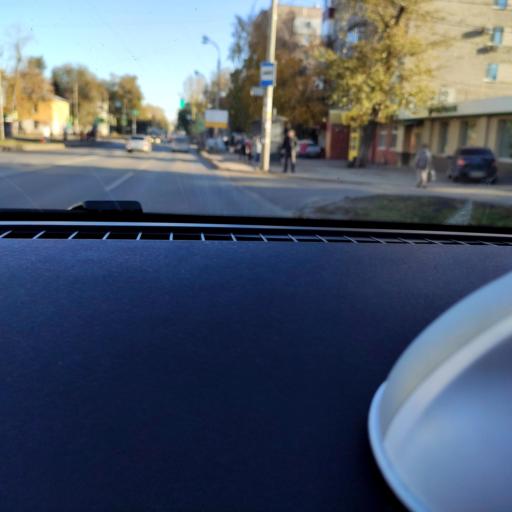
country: RU
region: Samara
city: Samara
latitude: 53.1963
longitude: 50.2198
